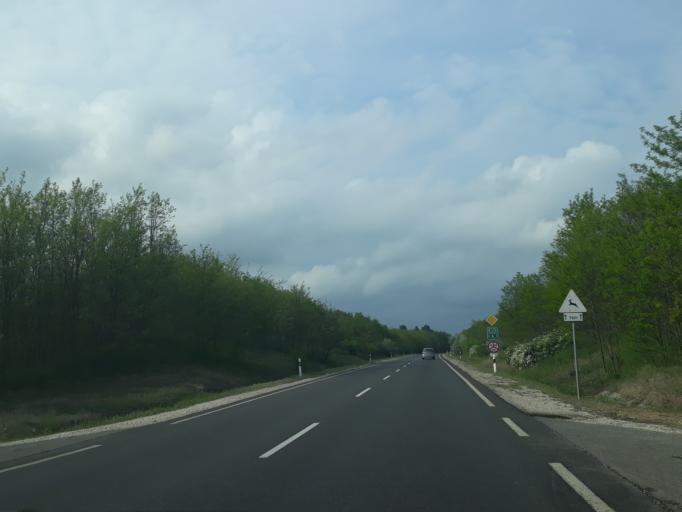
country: HU
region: Szabolcs-Szatmar-Bereg
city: Nyirtass
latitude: 48.0967
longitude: 21.9872
